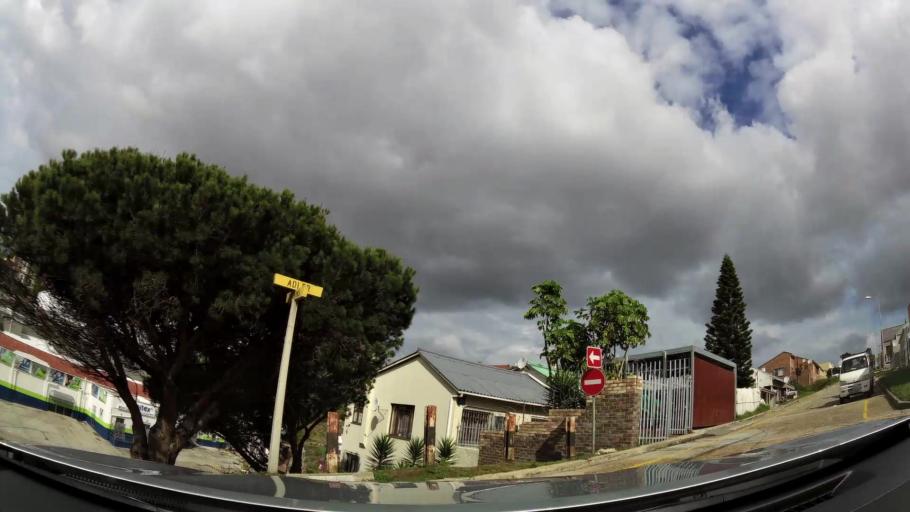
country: ZA
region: Eastern Cape
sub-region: Nelson Mandela Bay Metropolitan Municipality
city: Port Elizabeth
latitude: -33.9546
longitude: 25.6089
